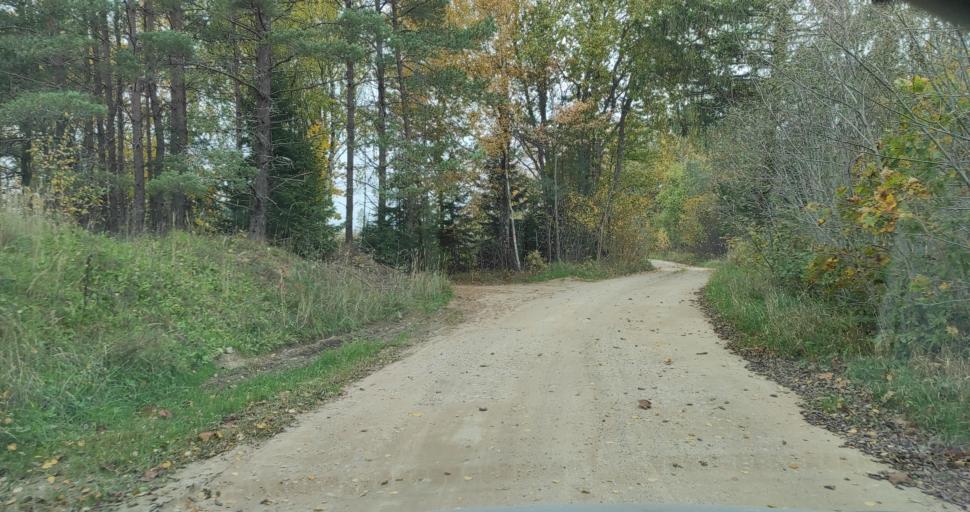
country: LV
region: Alsunga
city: Alsunga
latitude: 57.0373
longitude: 21.7119
